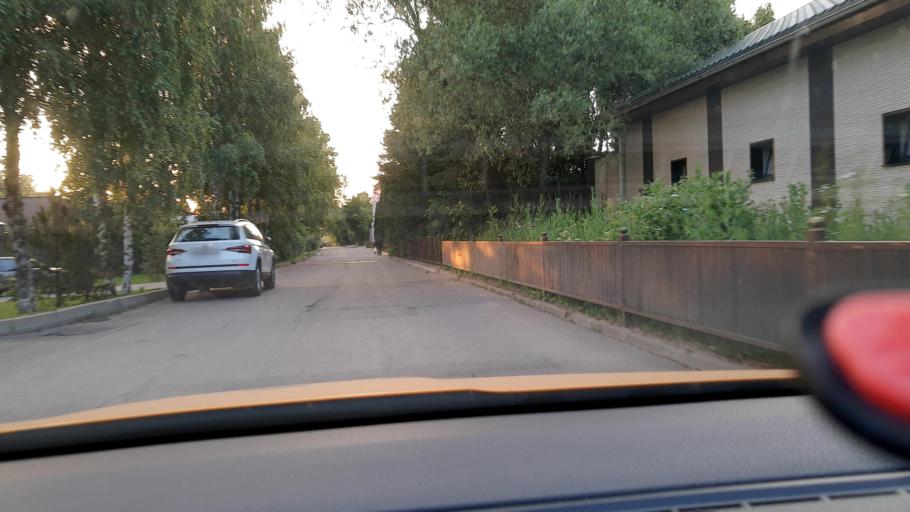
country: RU
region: Moskovskaya
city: Barvikha
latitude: 55.7246
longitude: 37.2977
